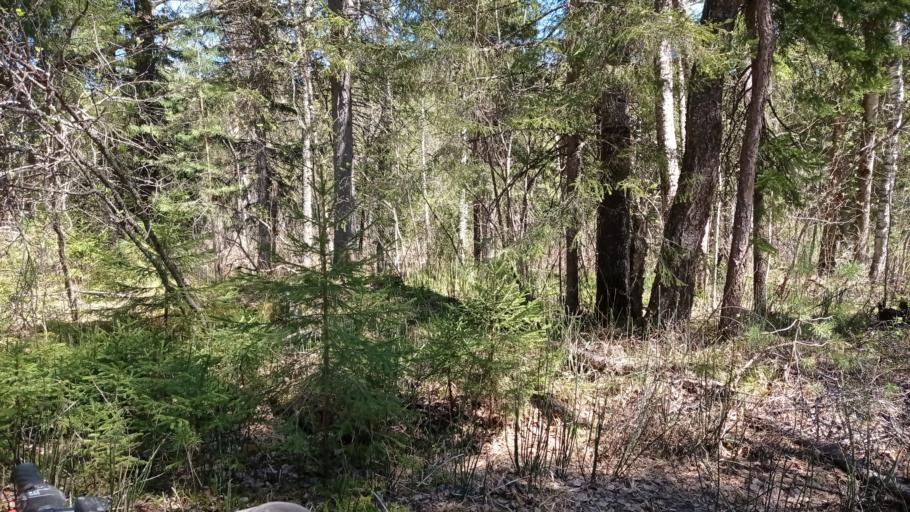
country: RU
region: Tomsk
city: Timiryazevskoye
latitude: 56.3917
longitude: 84.7422
